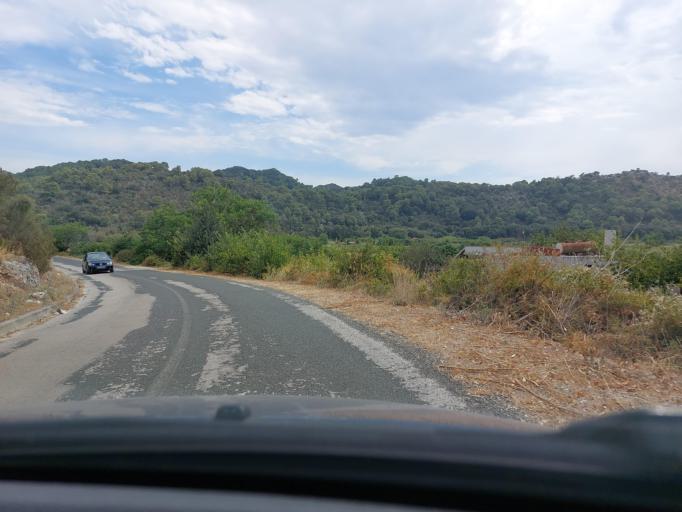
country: HR
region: Dubrovacko-Neretvanska
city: Smokvica
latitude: 42.7636
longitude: 16.8957
